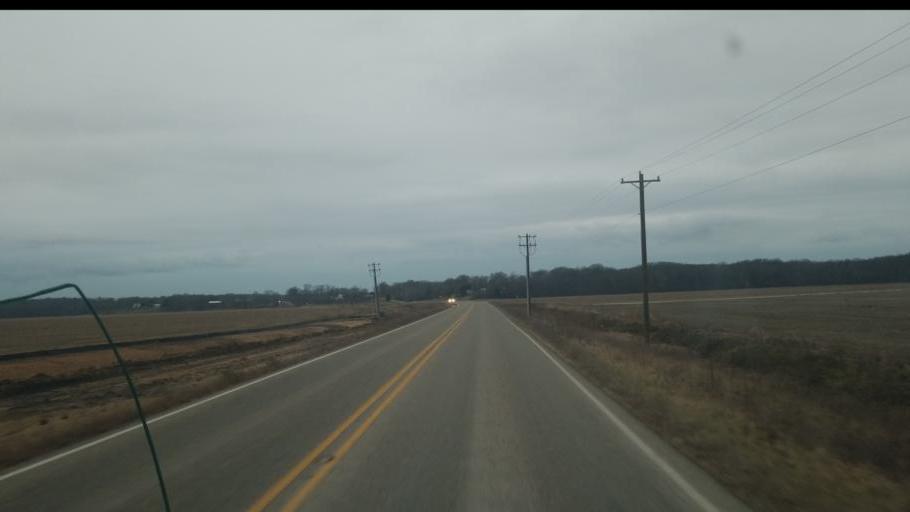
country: US
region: Indiana
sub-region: Clay County
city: Middlebury
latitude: 39.3851
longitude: -87.0239
